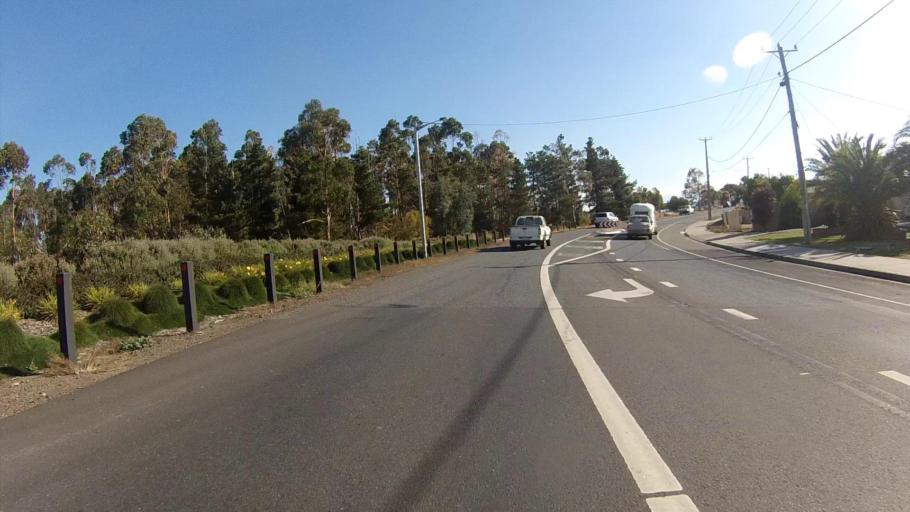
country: AU
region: Tasmania
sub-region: Sorell
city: Sorell
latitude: -42.7907
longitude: 147.5613
